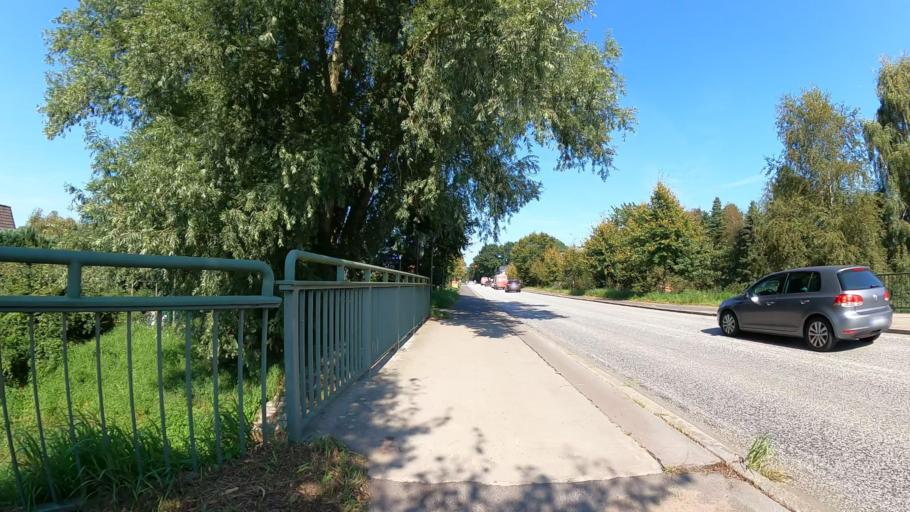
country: DE
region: Schleswig-Holstein
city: Lentfohrden
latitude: 53.8721
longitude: 9.8885
